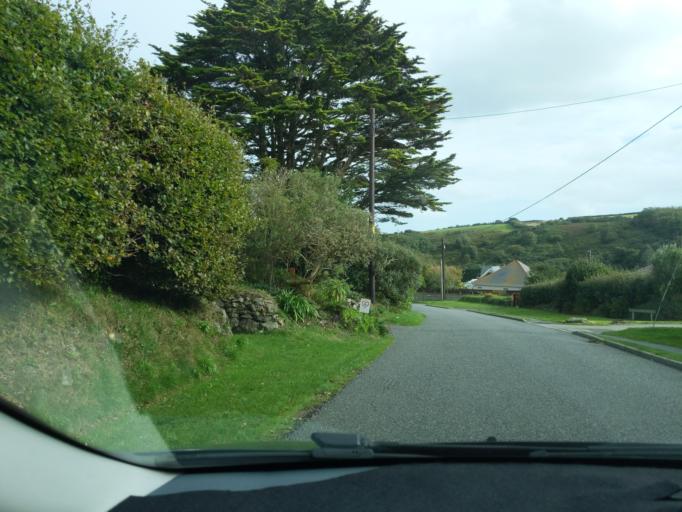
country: GB
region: England
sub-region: Cornwall
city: Mevagissey
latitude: 50.2409
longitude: -4.7974
